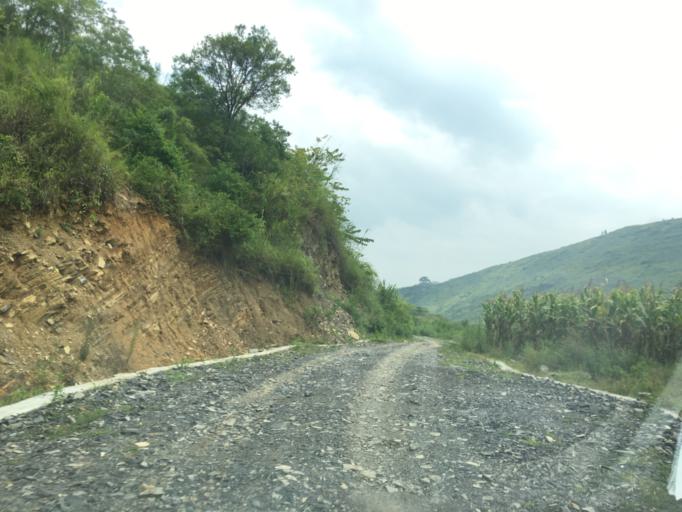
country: CN
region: Guangxi Zhuangzu Zizhiqu
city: Xinzhou
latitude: 25.1948
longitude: 105.7334
